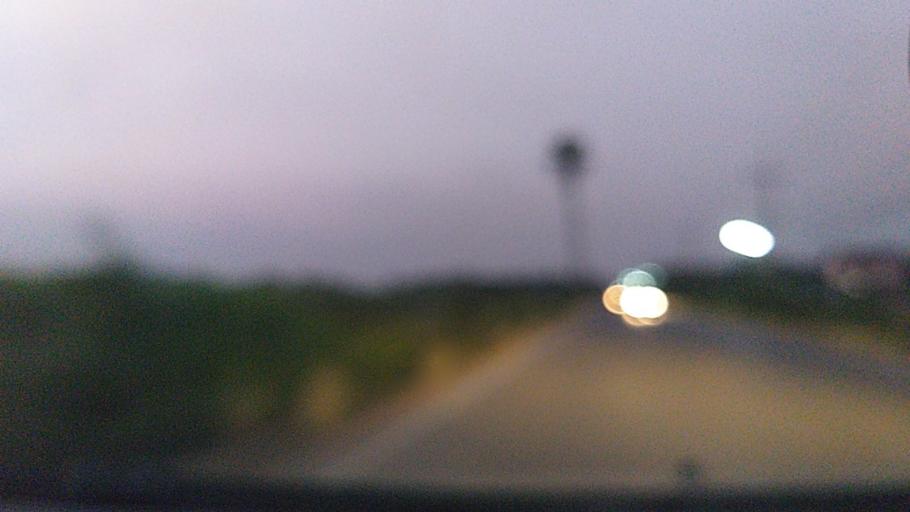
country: TH
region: Sing Buri
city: Sing Buri
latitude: 14.8402
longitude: 100.3936
